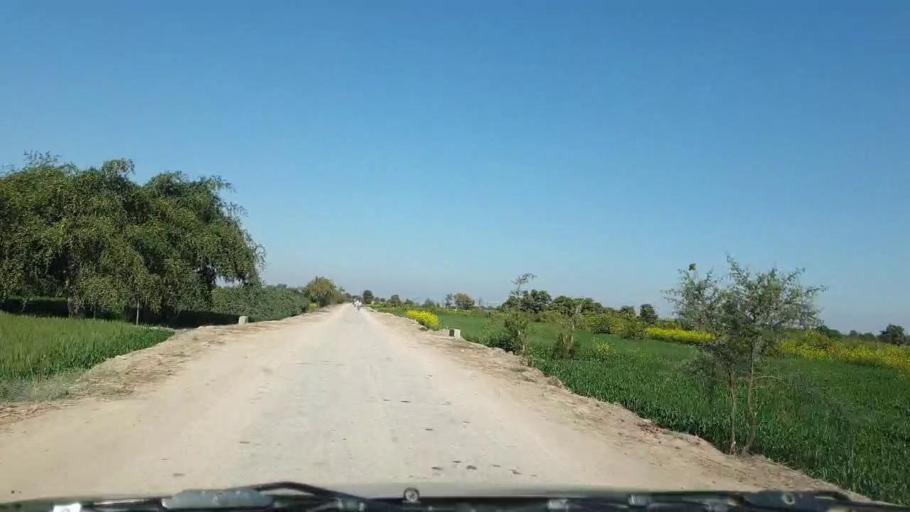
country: PK
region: Sindh
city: Khadro
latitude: 26.1352
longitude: 68.8161
